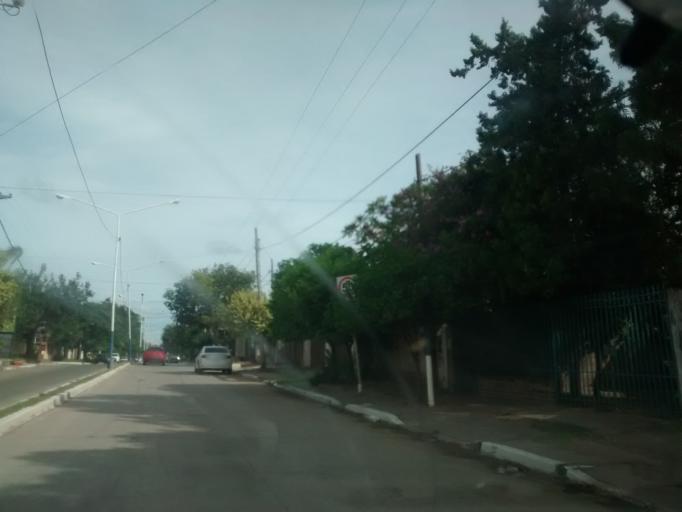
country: AR
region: Chaco
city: Resistencia
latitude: -27.4356
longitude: -58.9898
